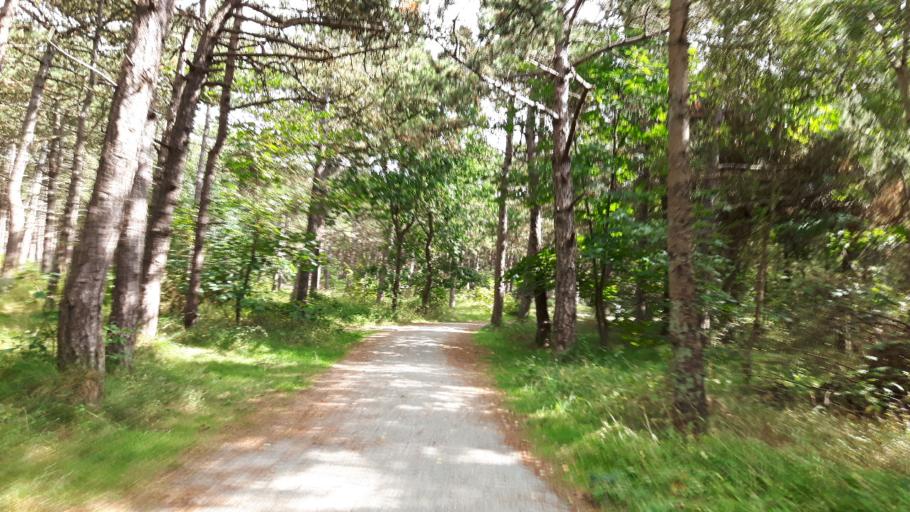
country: NL
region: Friesland
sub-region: Gemeente Ameland
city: Hollum
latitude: 53.4454
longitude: 5.6186
